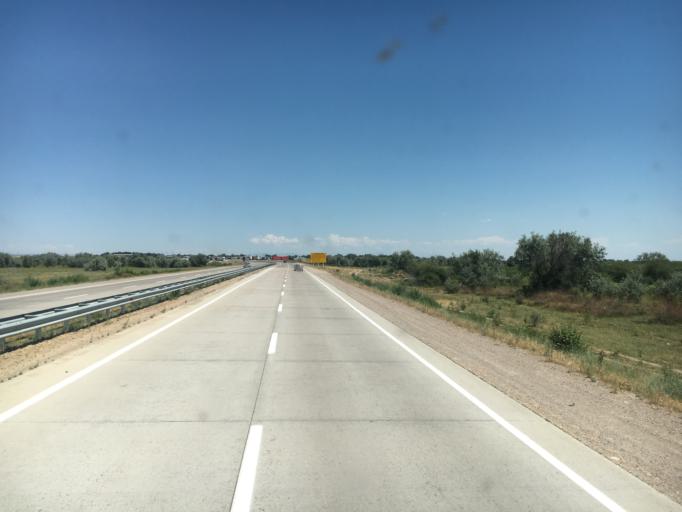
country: KG
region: Chuy
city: Sokuluk
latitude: 43.2678
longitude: 74.2125
